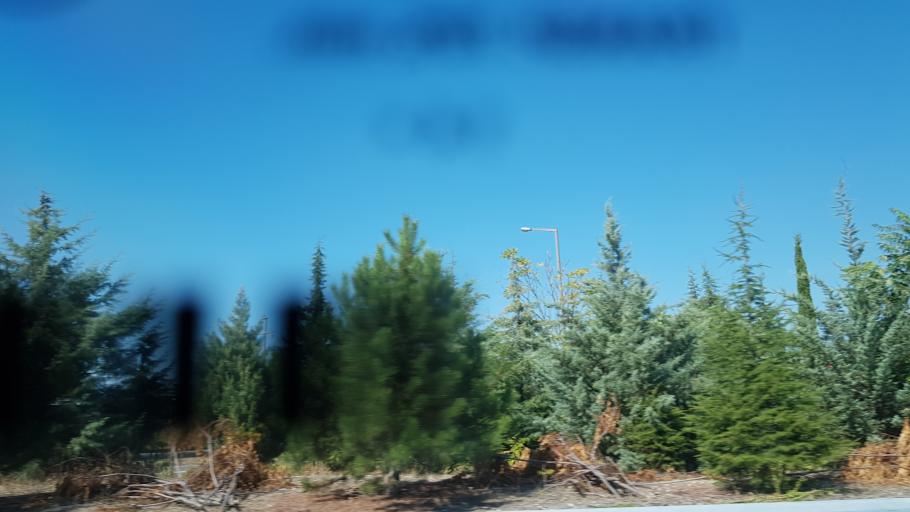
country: TR
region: Kirklareli
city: Luleburgaz
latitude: 41.3927
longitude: 27.3825
